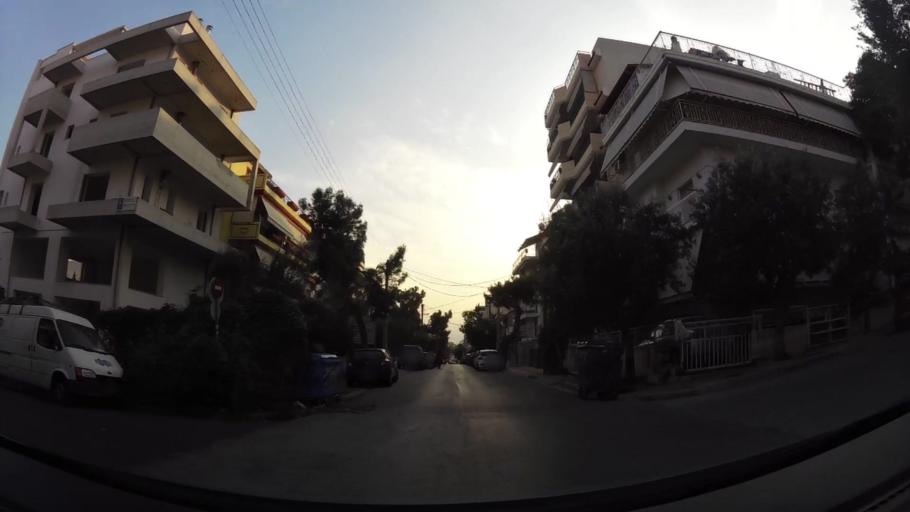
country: GR
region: Attica
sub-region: Nomarchia Athinas
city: Petroupolis
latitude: 38.0393
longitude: 23.6875
